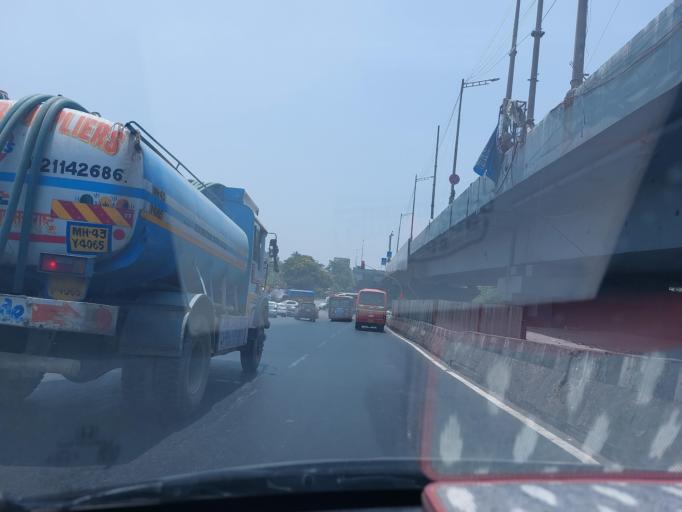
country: IN
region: Maharashtra
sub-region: Mumbai Suburban
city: Mumbai
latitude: 19.0711
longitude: 72.9080
